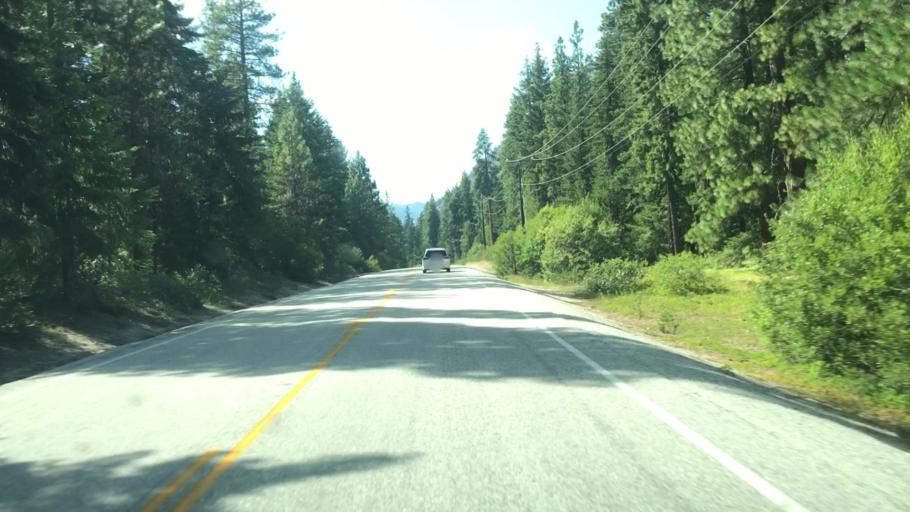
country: US
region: Washington
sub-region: Chelan County
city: Leavenworth
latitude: 47.8225
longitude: -120.7501
